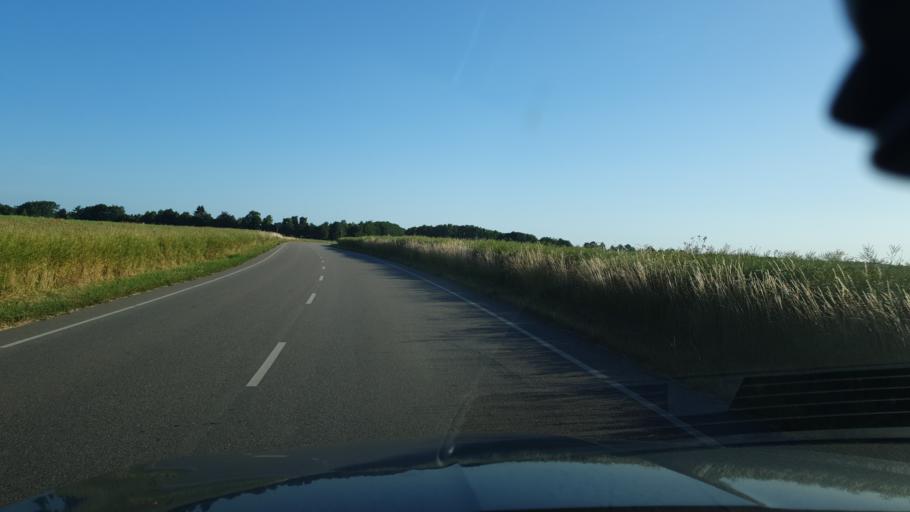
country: DK
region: Zealand
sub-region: Soro Kommune
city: Frederiksberg
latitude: 55.4028
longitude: 11.5637
